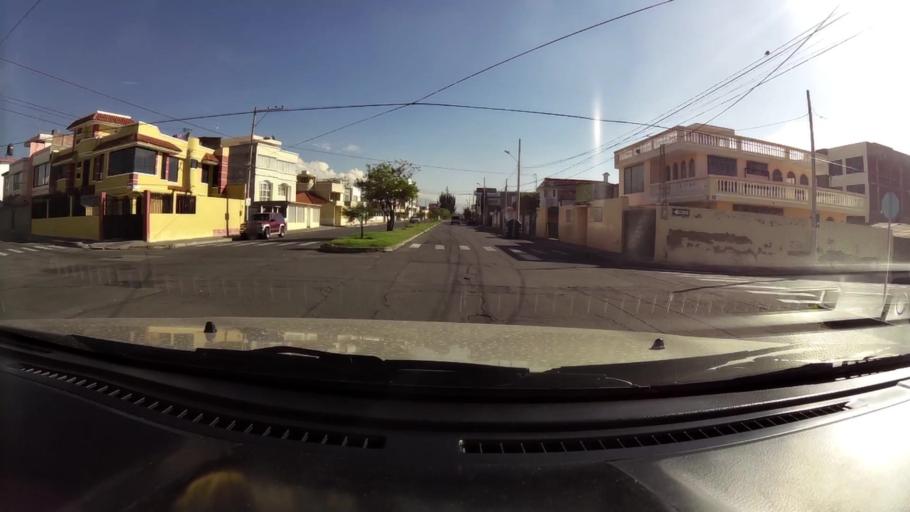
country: EC
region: Chimborazo
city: Riobamba
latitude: -1.6511
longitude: -78.6662
